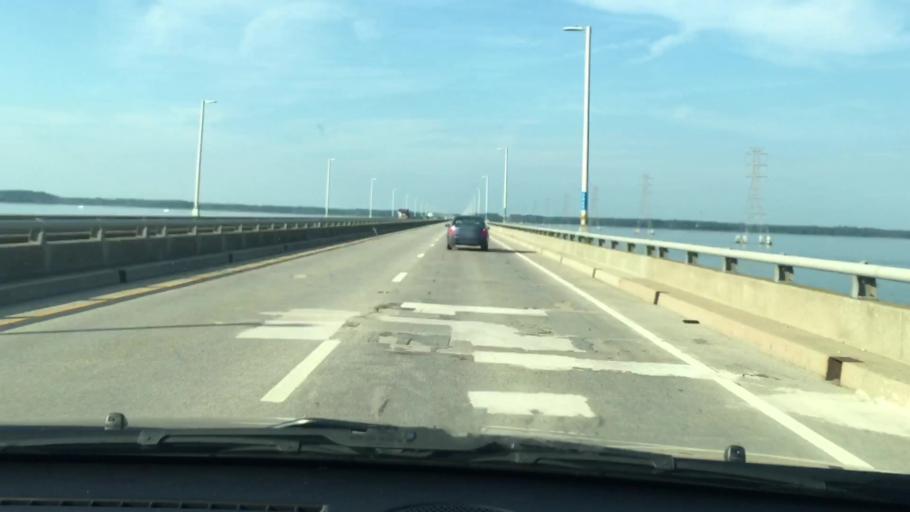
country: US
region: Virginia
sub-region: City of Newport News
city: Newport News
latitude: 36.9867
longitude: -76.4886
